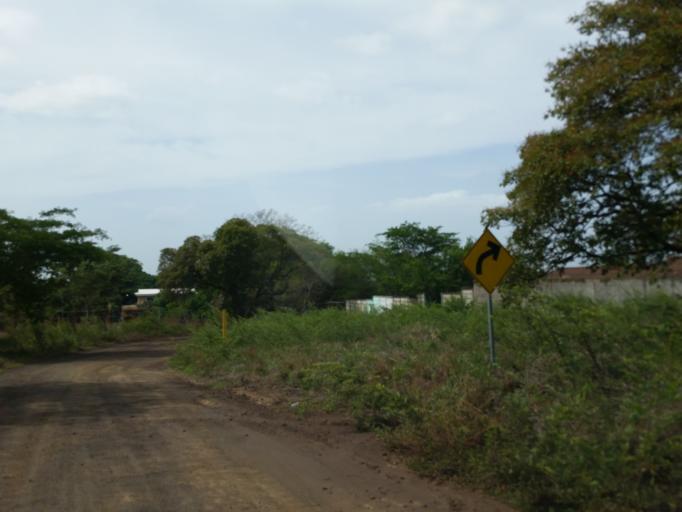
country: NI
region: Managua
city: Managua
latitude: 12.1057
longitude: -86.2591
